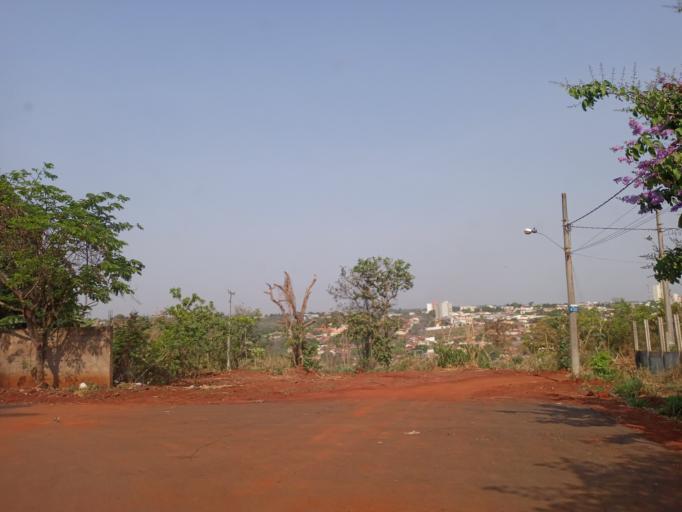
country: BR
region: Minas Gerais
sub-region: Ituiutaba
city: Ituiutaba
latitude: -18.9604
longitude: -49.4752
